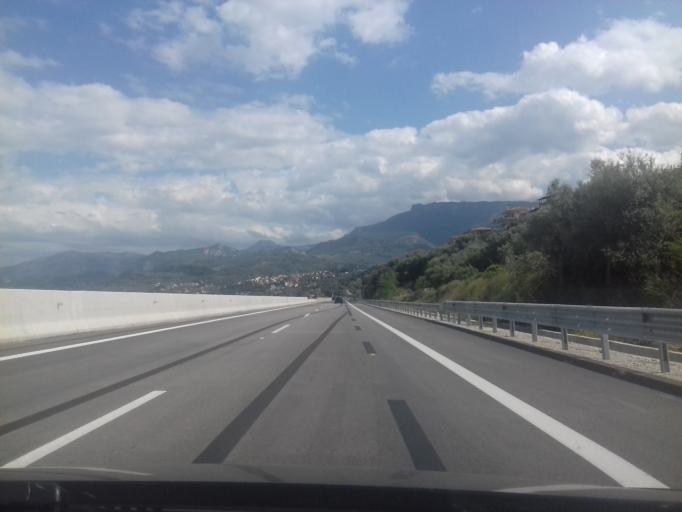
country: GR
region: West Greece
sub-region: Nomos Achaias
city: Siliveniotika
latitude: 38.1626
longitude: 22.3359
